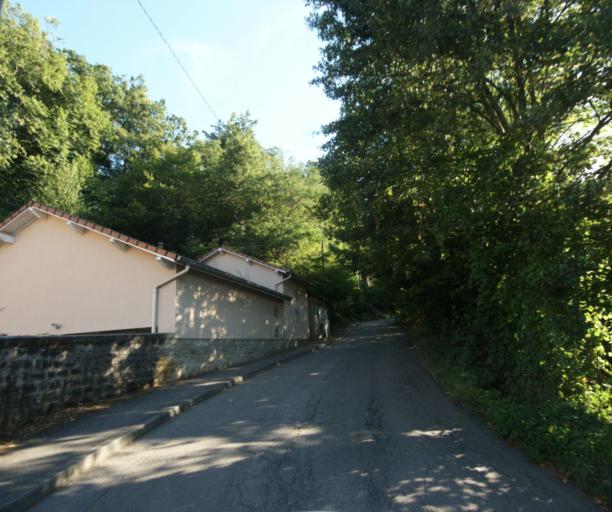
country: FR
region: Lorraine
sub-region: Departement des Vosges
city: Chantraine
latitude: 48.1515
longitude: 6.4506
